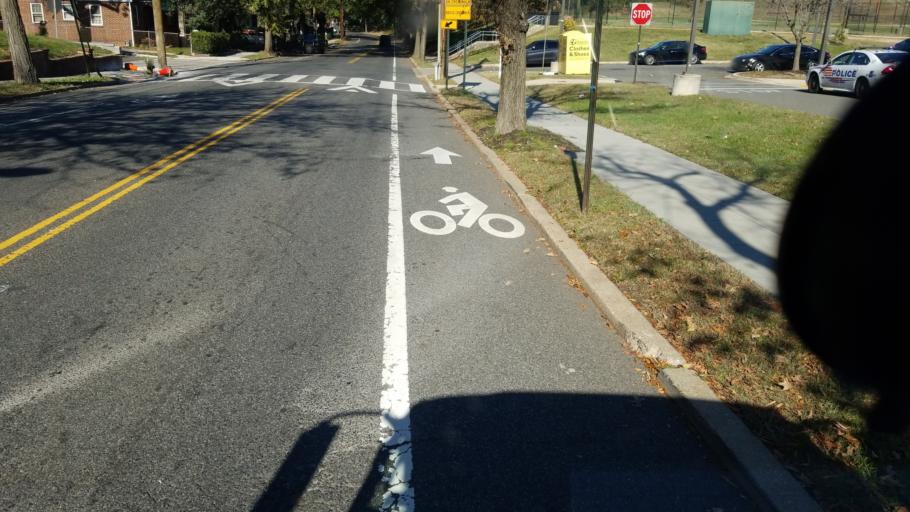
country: US
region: Maryland
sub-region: Prince George's County
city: Fairmount Heights
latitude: 38.8937
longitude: -76.9329
